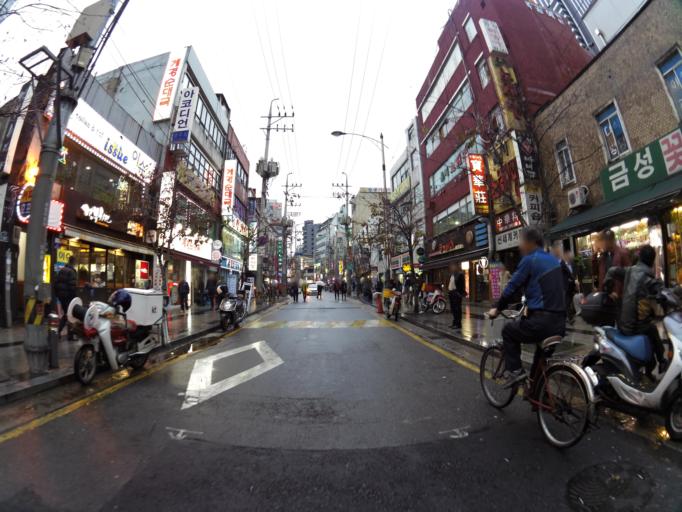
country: KR
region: Seoul
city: Seoul
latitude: 37.5705
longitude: 126.9897
